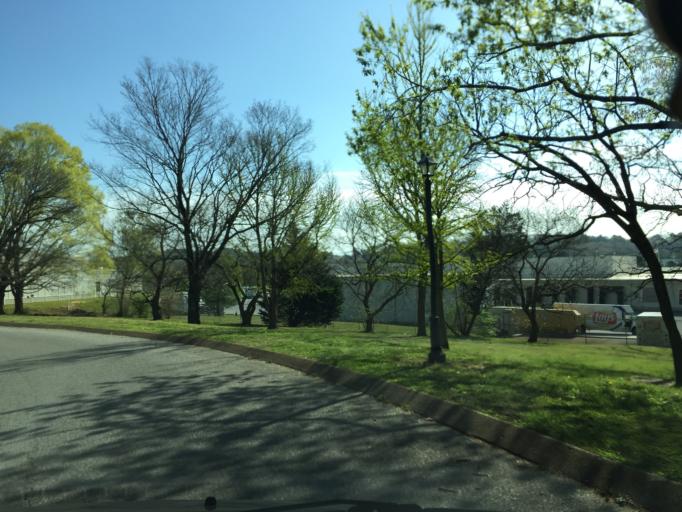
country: US
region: Tennessee
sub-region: Hamilton County
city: Harrison
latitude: 35.0725
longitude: -85.1830
